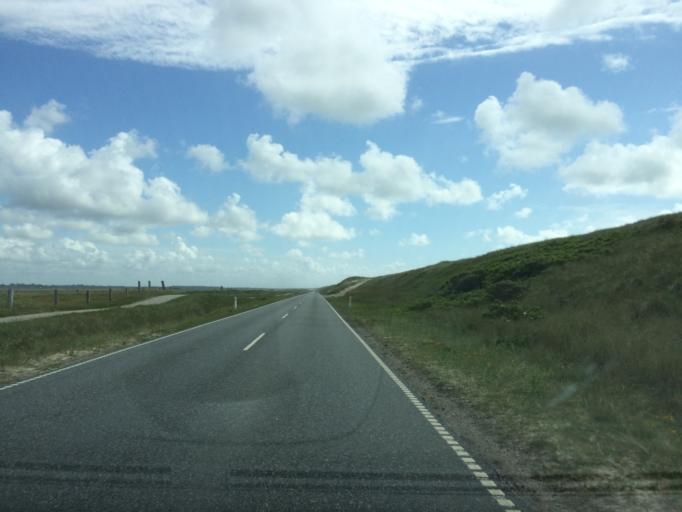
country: DK
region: Central Jutland
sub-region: Holstebro Kommune
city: Ulfborg
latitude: 56.3518
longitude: 8.1224
